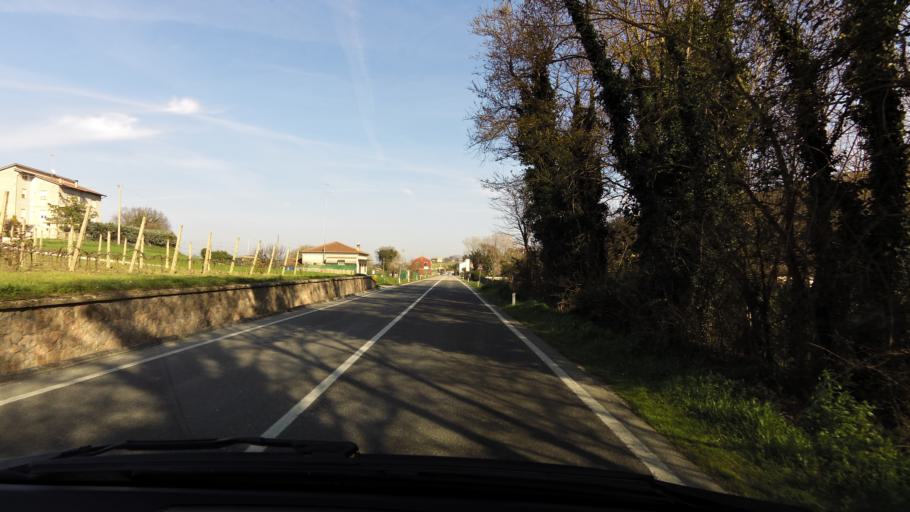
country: IT
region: The Marches
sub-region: Provincia di Ancona
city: Villa Musone
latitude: 43.4704
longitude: 13.5882
